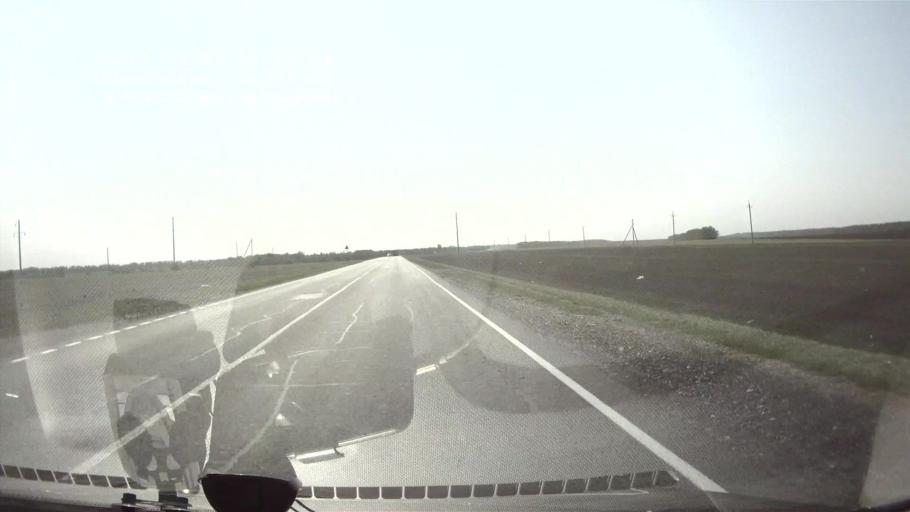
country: RU
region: Krasnodarskiy
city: Novopokrovskaya
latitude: 45.9179
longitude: 40.7161
